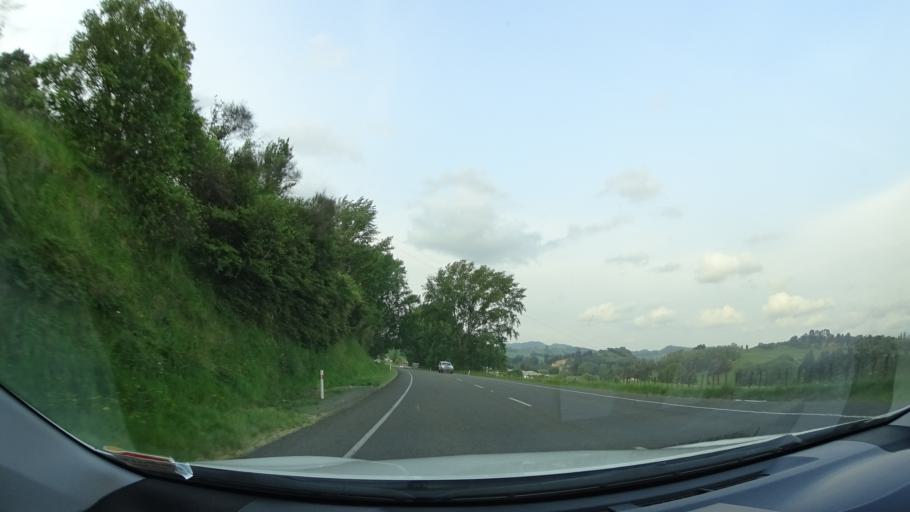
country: NZ
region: Manawatu-Wanganui
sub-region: Ruapehu District
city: Waiouru
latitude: -39.7396
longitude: 175.8397
